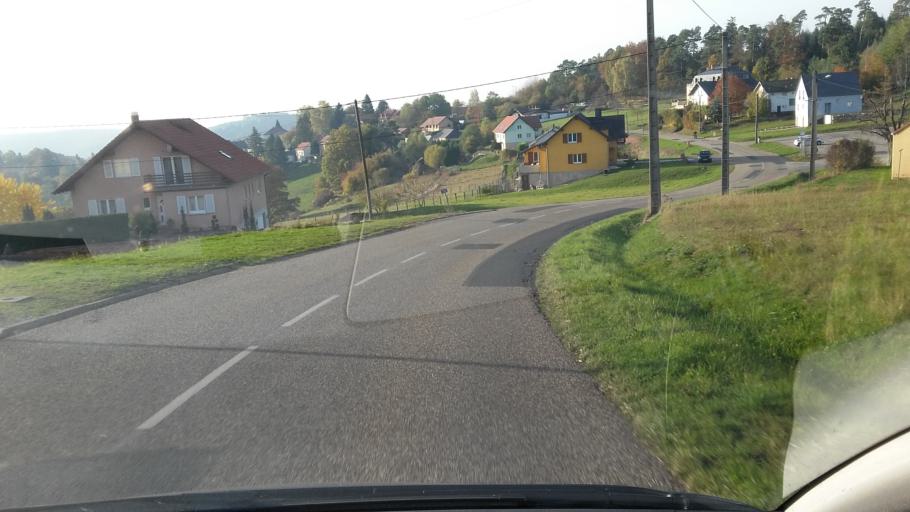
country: FR
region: Lorraine
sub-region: Departement de la Moselle
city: Dabo
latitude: 48.6860
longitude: 7.2150
